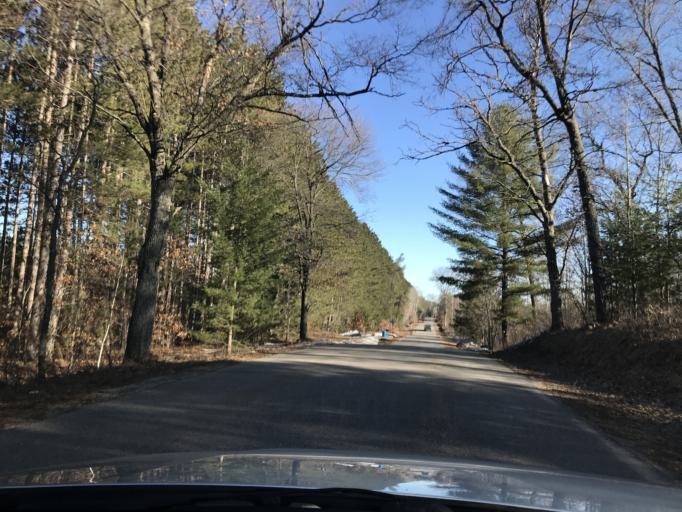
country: US
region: Wisconsin
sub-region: Marinette County
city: Niagara
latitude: 45.3926
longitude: -88.0790
